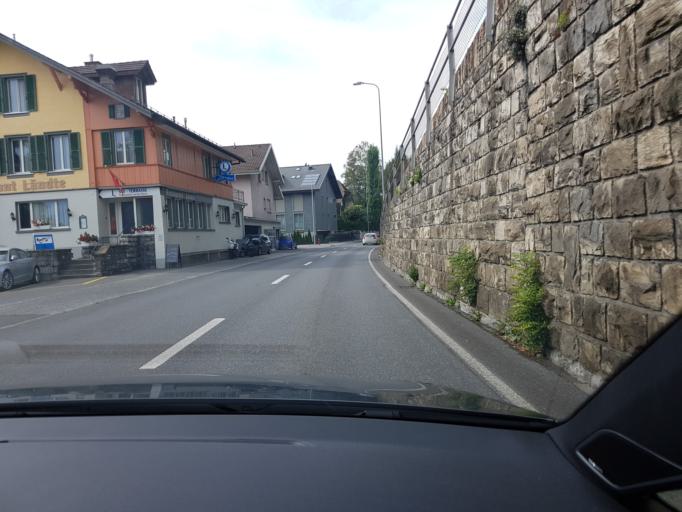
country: CH
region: Bern
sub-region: Thun District
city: Hilterfingen
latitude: 46.7315
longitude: 7.6641
